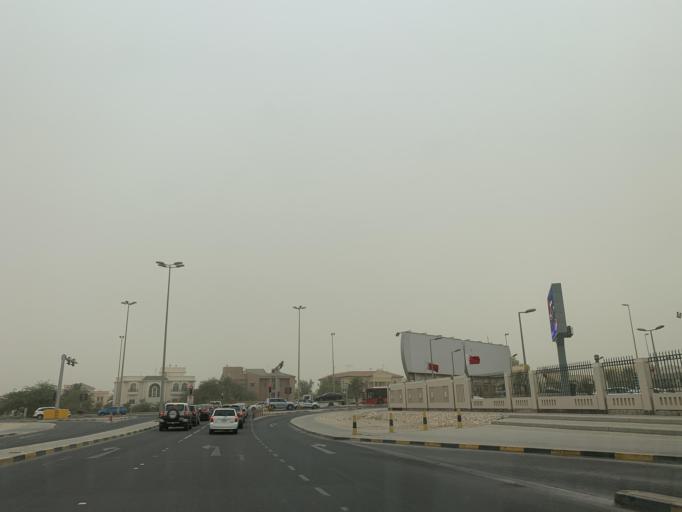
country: BH
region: Central Governorate
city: Madinat Hamad
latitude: 26.1369
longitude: 50.5213
